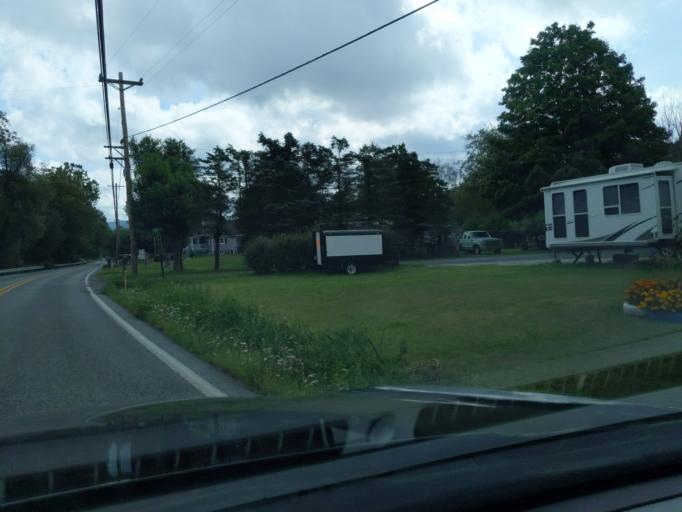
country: US
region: Pennsylvania
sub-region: Blair County
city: Duncansville
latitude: 40.3890
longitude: -78.4635
